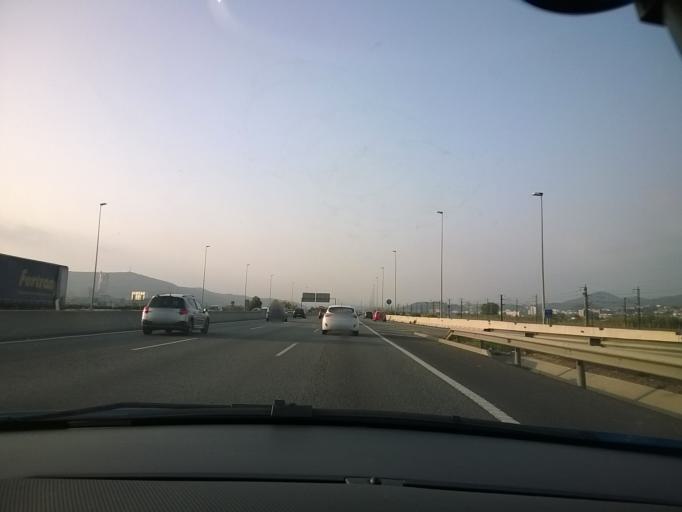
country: ES
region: Catalonia
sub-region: Provincia de Barcelona
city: Sant Vicenc dels Horts
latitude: 41.3917
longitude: 2.0183
